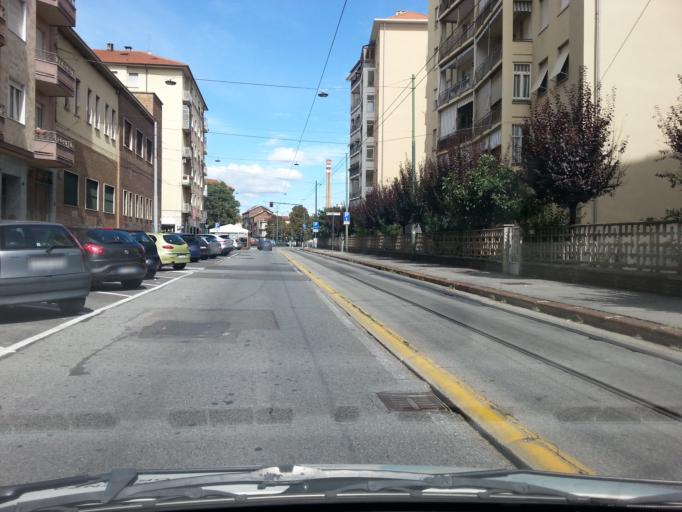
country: IT
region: Piedmont
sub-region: Provincia di Torino
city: Turin
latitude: 45.0357
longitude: 7.6710
